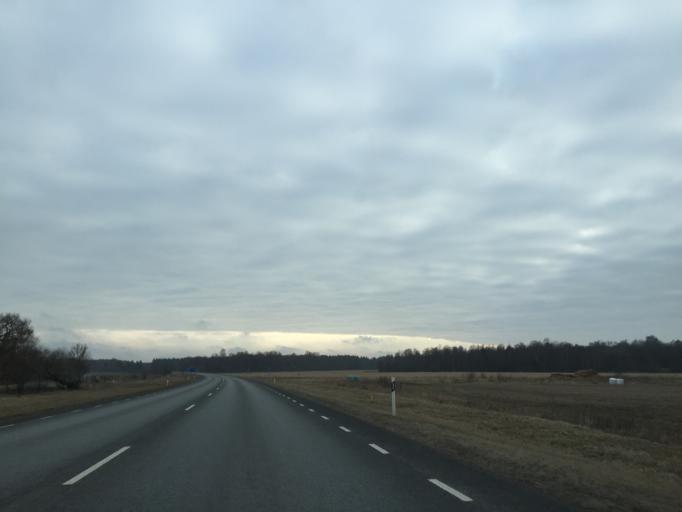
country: EE
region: Saare
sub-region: Orissaare vald
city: Orissaare
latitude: 58.5139
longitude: 22.8782
